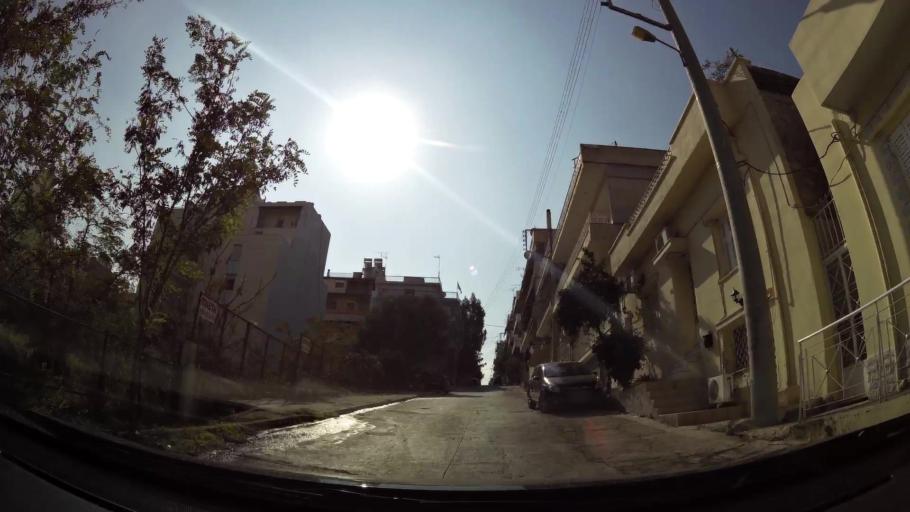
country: GR
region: Attica
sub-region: Nomos Piraios
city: Keratsini
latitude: 37.9550
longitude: 23.6158
